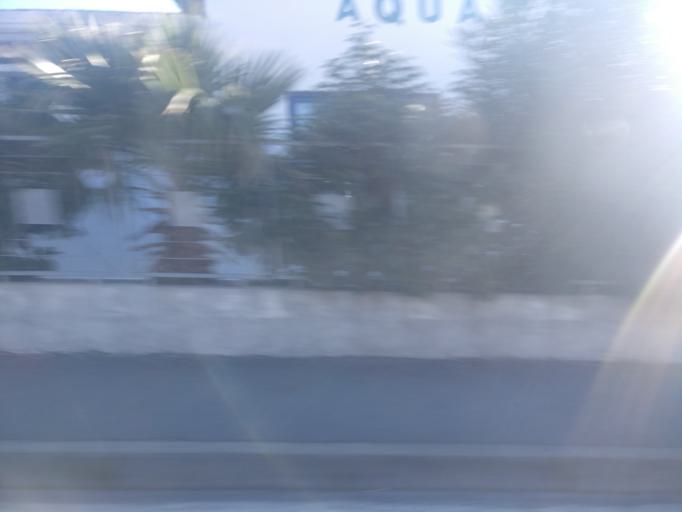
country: IT
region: Liguria
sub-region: Provincia di Savona
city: Valleggia
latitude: 44.2865
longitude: 8.4484
